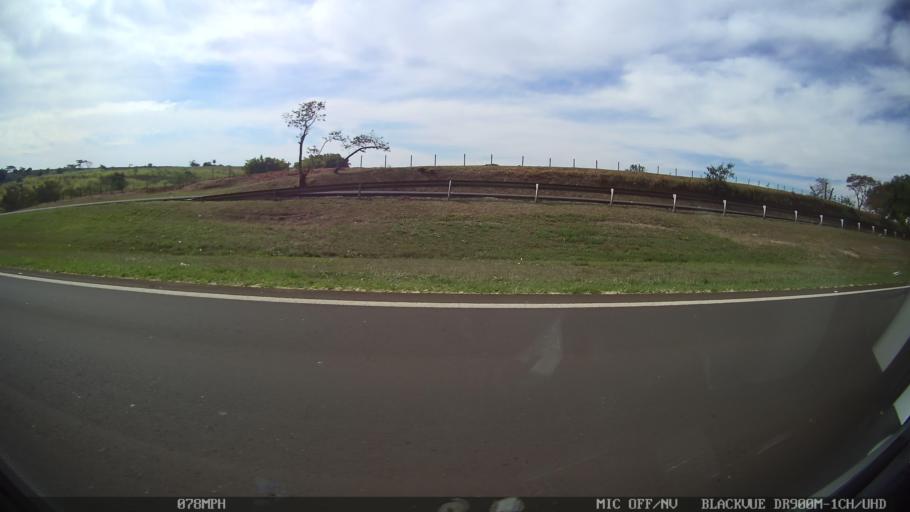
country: BR
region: Sao Paulo
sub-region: Matao
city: Matao
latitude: -21.6043
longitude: -48.4295
